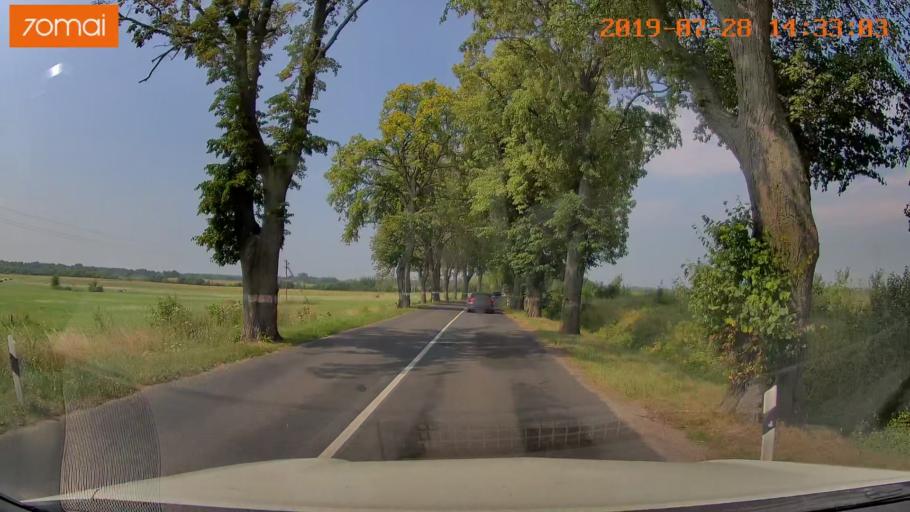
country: RU
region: Kaliningrad
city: Primorsk
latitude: 54.8167
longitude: 20.0355
